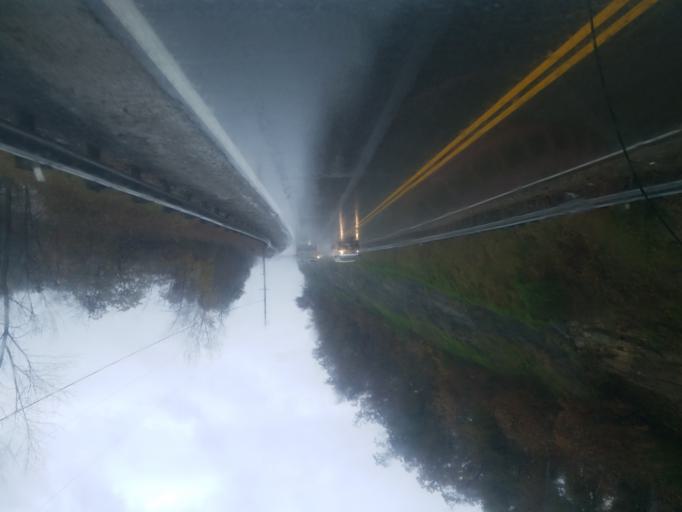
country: US
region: Ohio
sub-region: Muskingum County
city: Pleasant Grove
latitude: 39.8575
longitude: -81.8995
